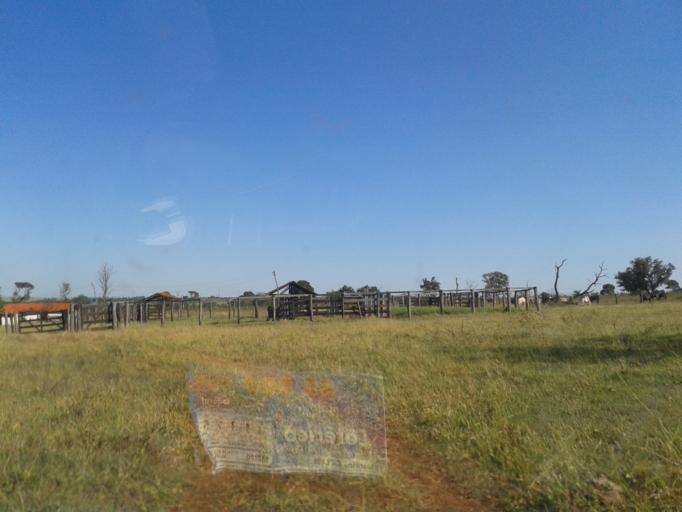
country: BR
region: Minas Gerais
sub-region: Santa Vitoria
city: Santa Vitoria
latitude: -19.0415
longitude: -50.3819
